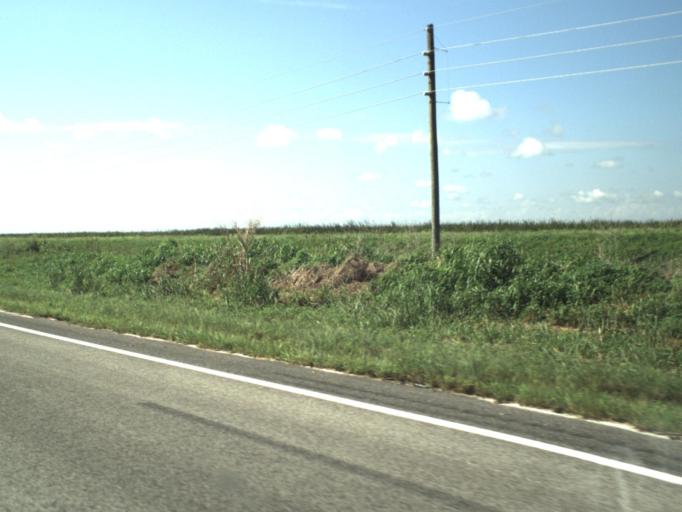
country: US
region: Florida
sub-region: Palm Beach County
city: Belle Glade Camp
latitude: 26.3838
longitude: -80.5758
